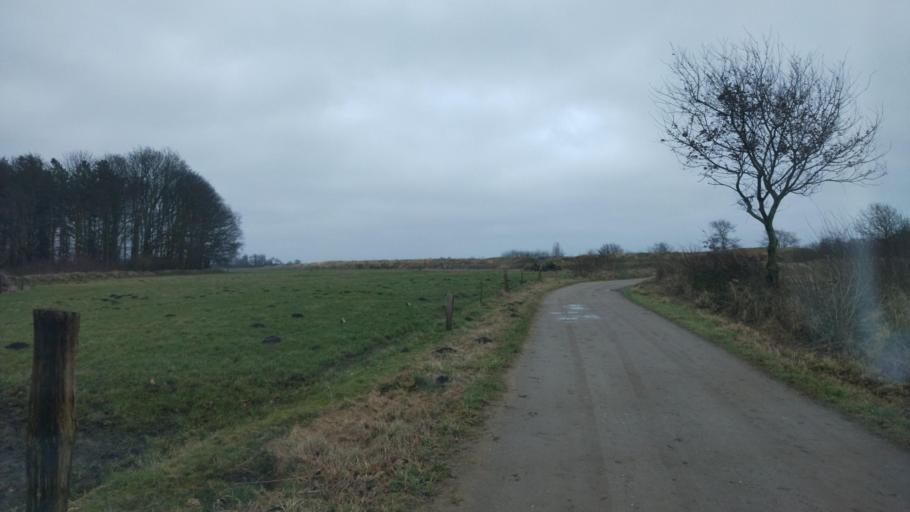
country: DE
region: Schleswig-Holstein
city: Gross Rheide
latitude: 54.4593
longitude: 9.4324
